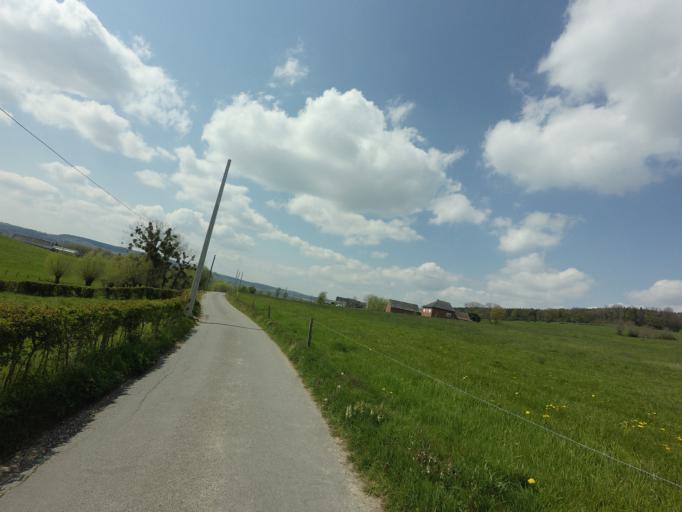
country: BE
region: Wallonia
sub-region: Province de Liege
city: Plombieres
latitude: 50.7555
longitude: 5.9637
